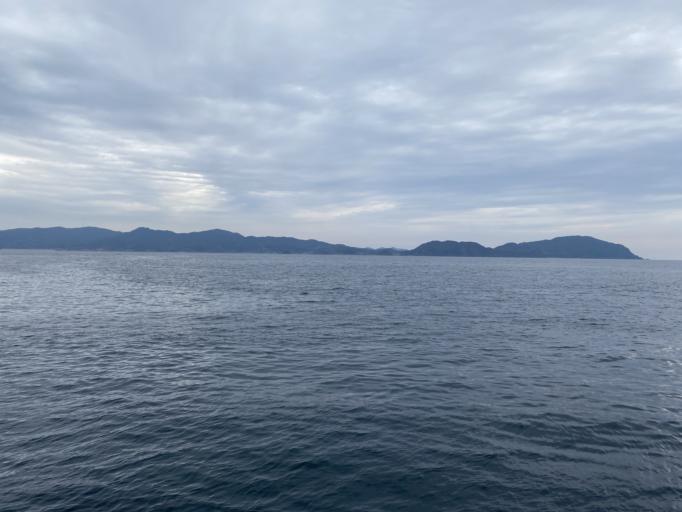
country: JP
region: Nagasaki
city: Nagasaki-shi
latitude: 32.6269
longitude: 129.7326
